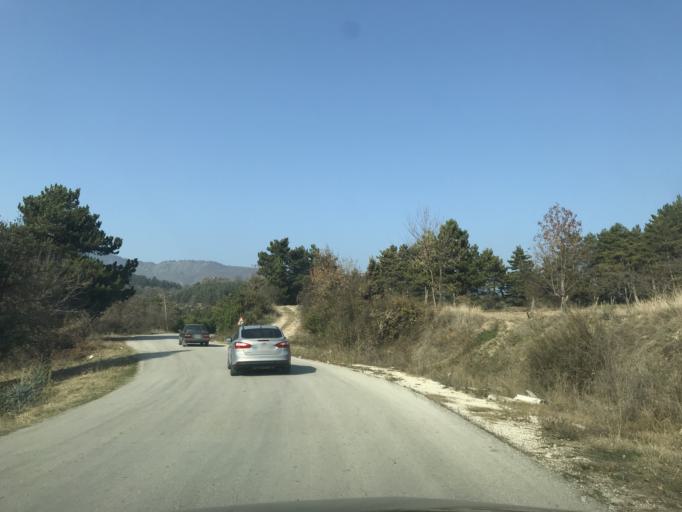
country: TR
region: Bolu
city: Bolu
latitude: 40.7798
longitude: 31.6326
